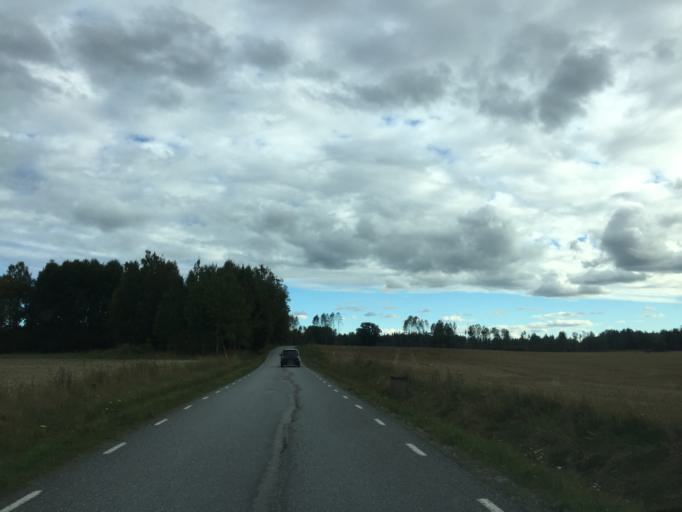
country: SE
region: OErebro
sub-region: Orebro Kommun
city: Hovsta
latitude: 59.3407
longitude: 15.1723
